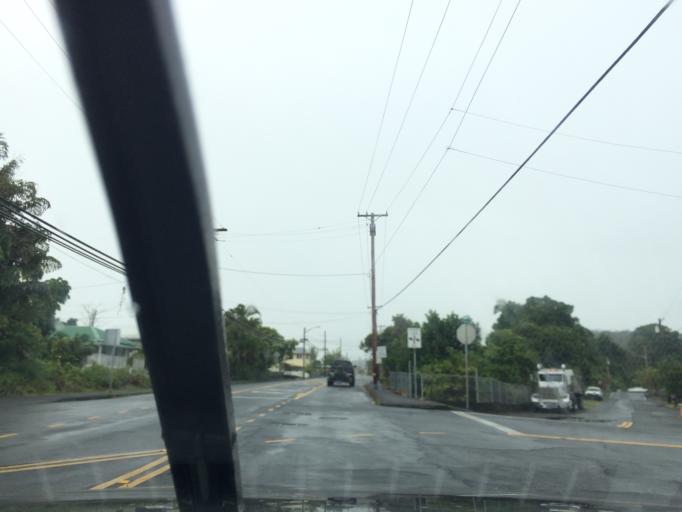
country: US
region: Hawaii
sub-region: Hawaii County
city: Hilo
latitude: 19.7156
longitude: -155.1042
